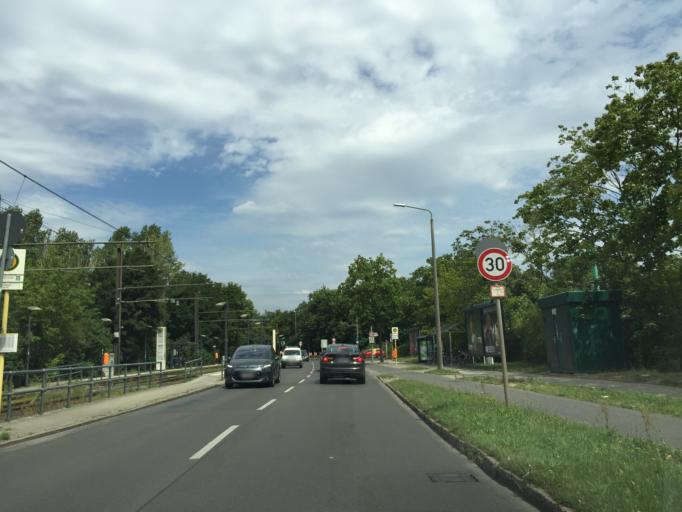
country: DE
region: Berlin
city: Mahlsdorf
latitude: 52.4979
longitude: 13.6127
